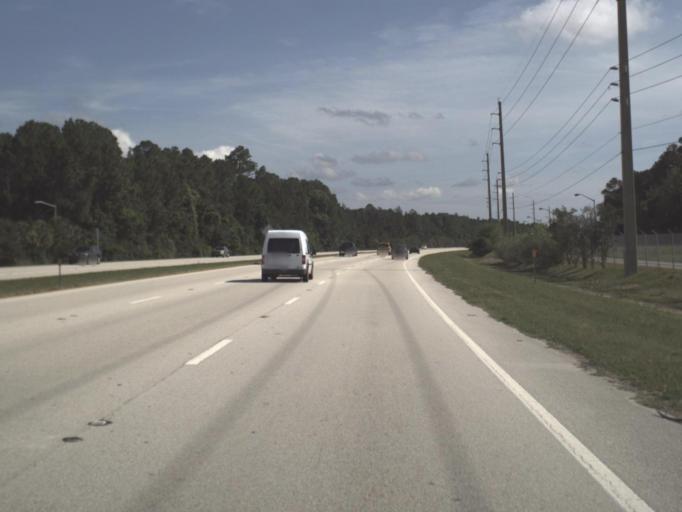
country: US
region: Florida
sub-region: Clay County
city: Orange Park
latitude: 30.1993
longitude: -81.7078
